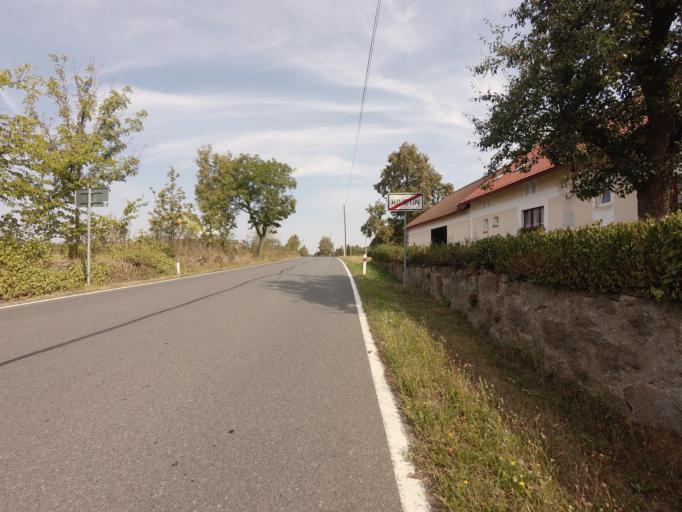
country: CZ
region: Central Bohemia
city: Petrovice
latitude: 49.5442
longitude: 14.3474
